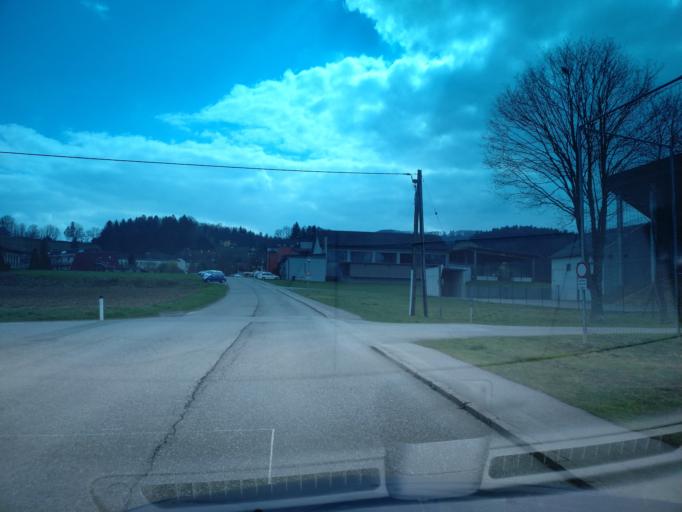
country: AT
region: Styria
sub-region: Politischer Bezirk Leibnitz
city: Grossklein
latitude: 46.7378
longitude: 15.4367
